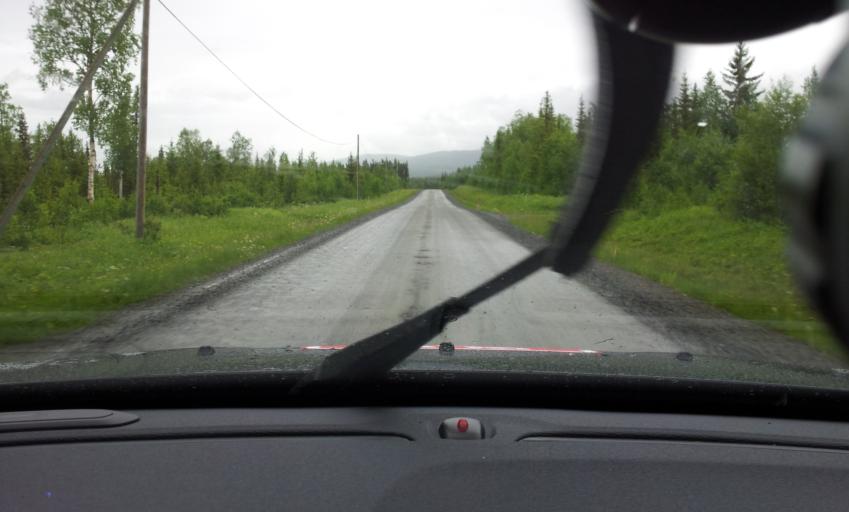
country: SE
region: Jaemtland
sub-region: Are Kommun
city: Are
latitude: 63.4371
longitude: 12.8071
